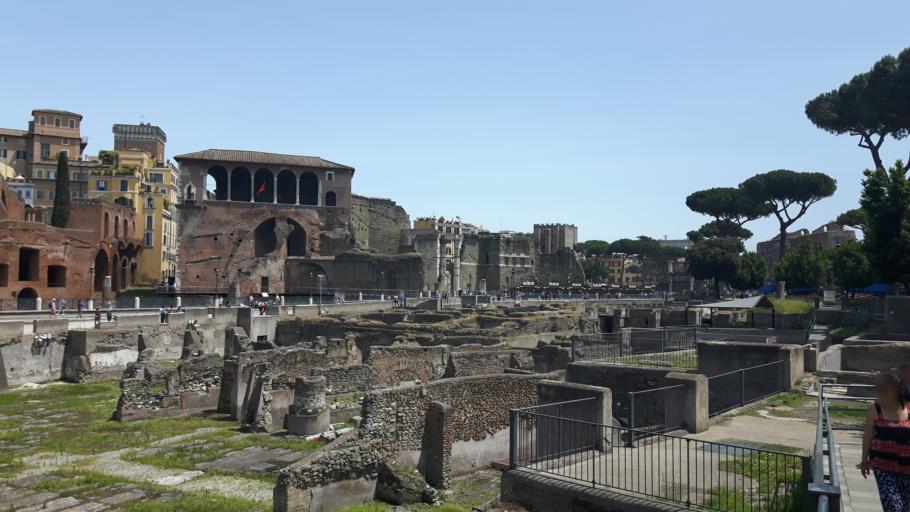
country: IT
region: Latium
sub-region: Citta metropolitana di Roma Capitale
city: Rome
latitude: 41.8949
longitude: 12.4848
